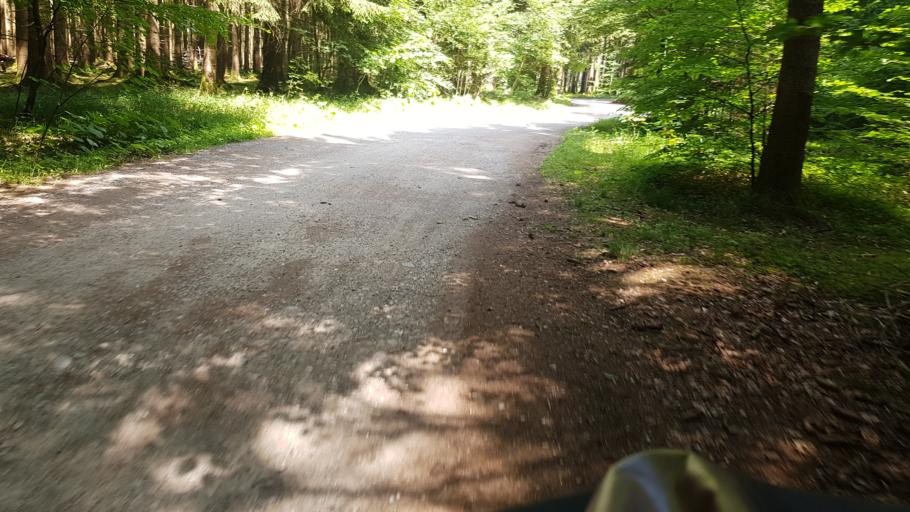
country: DE
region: Bavaria
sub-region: Upper Bavaria
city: Gauting
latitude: 48.0324
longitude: 11.3988
